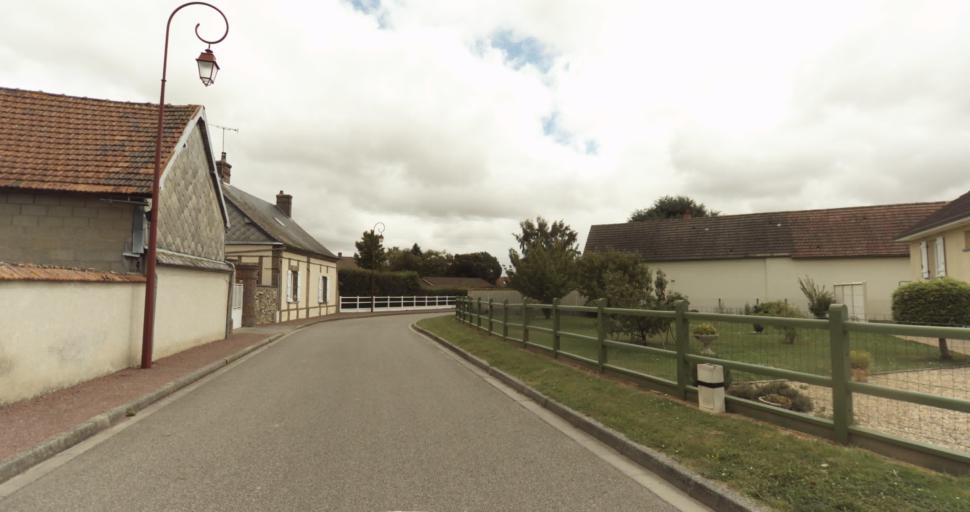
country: FR
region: Haute-Normandie
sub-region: Departement de l'Eure
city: Evreux
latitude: 48.9373
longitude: 1.1958
